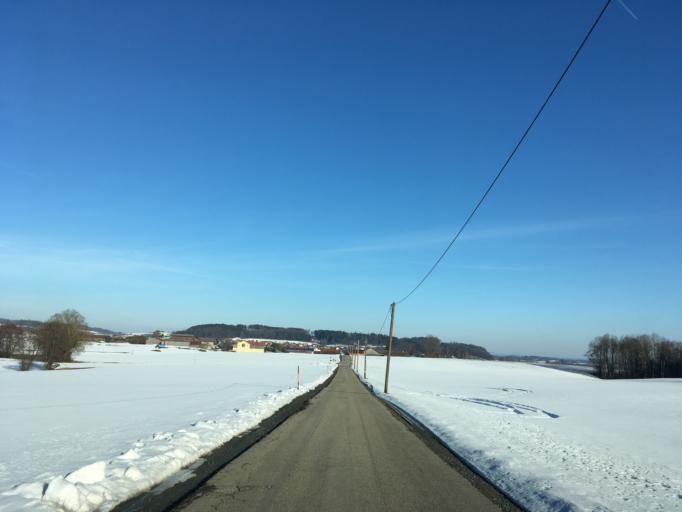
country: DE
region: Bavaria
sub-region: Upper Bavaria
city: Steinhoring
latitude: 48.0970
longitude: 12.0109
